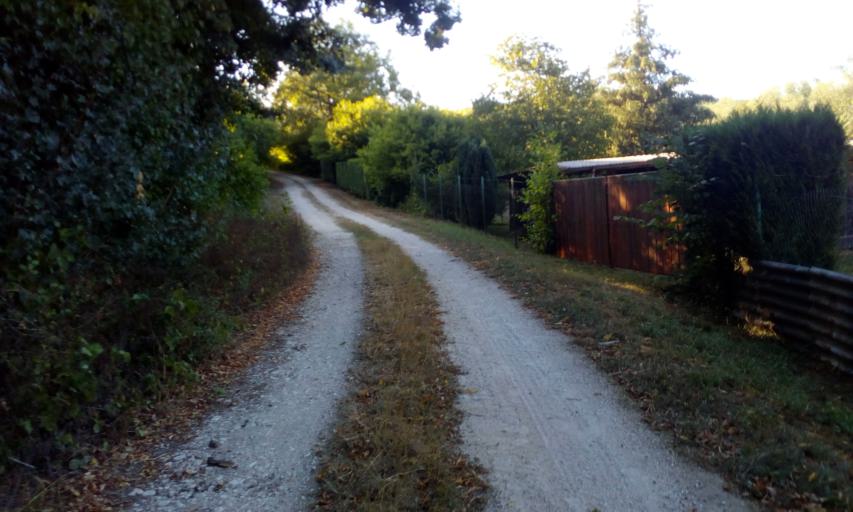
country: FR
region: Lorraine
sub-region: Departement de Meurthe-et-Moselle
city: Pagny-sur-Moselle
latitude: 48.9641
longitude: 5.8836
